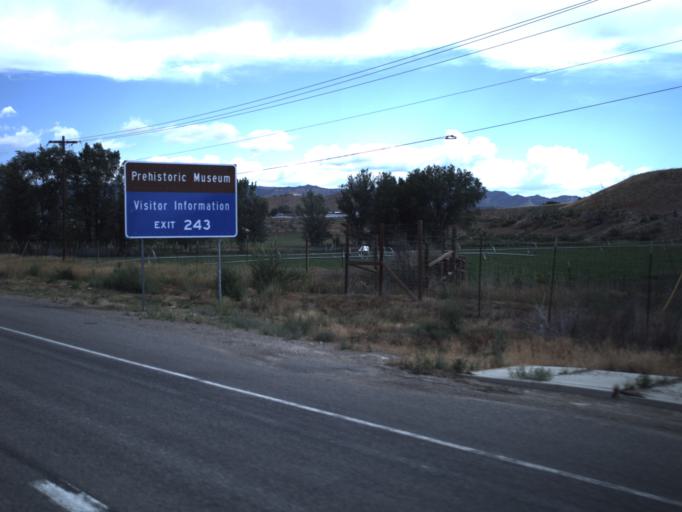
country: US
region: Utah
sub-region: Carbon County
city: Price
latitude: 39.5812
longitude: -110.7870
